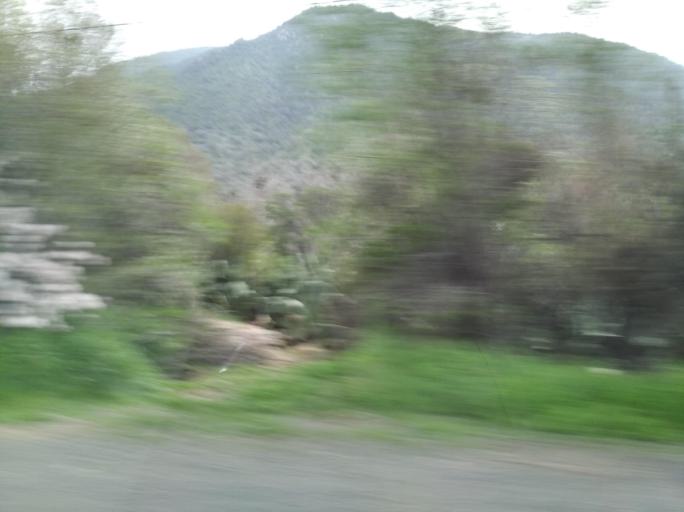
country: CL
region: Santiago Metropolitan
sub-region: Provincia de Chacabuco
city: Lampa
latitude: -33.0769
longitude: -70.9510
